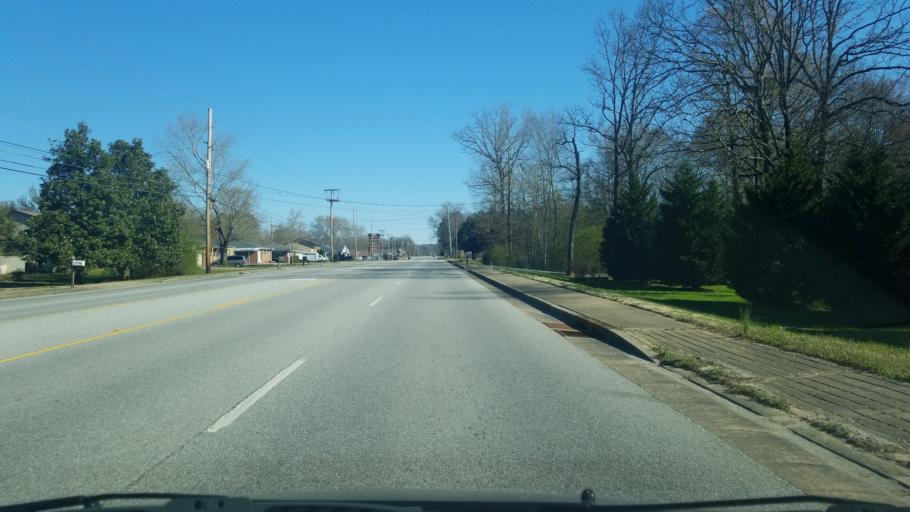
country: US
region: Tennessee
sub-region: Hamilton County
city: Middle Valley
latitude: 35.1842
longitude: -85.1689
